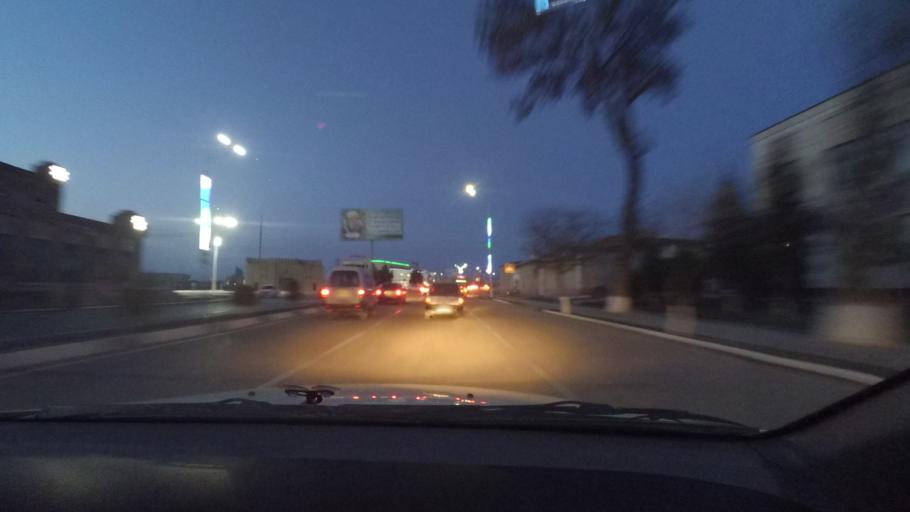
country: UZ
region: Bukhara
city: Bukhara
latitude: 39.7810
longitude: 64.4114
